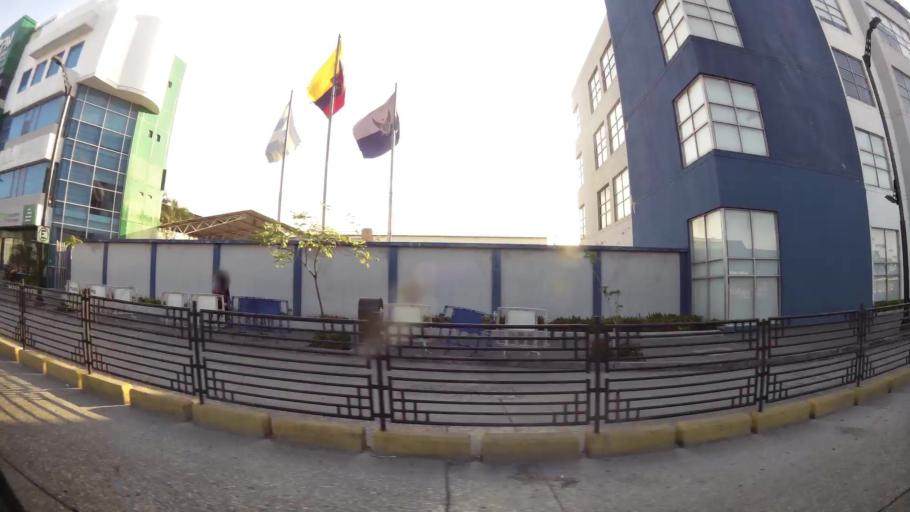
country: EC
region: Guayas
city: Guayaquil
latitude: -2.1765
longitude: -79.8921
